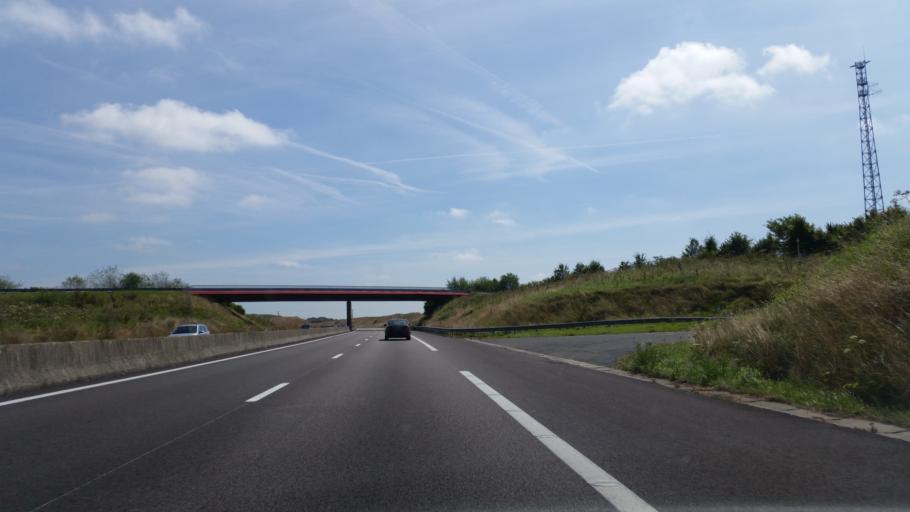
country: FR
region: Haute-Normandie
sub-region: Departement de la Seine-Maritime
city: Gaillefontaine
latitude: 49.7392
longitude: 1.6082
